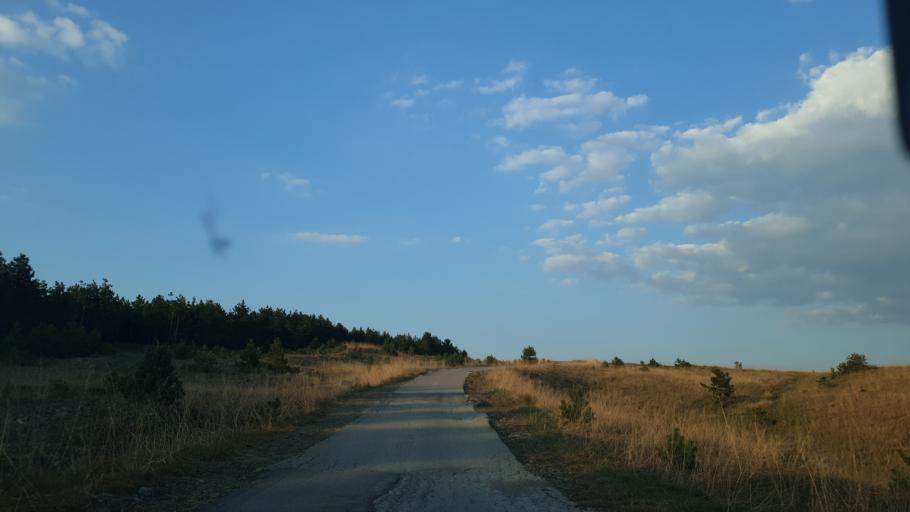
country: RS
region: Central Serbia
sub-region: Zlatiborski Okrug
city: Kosjeric
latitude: 44.0180
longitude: 20.0004
